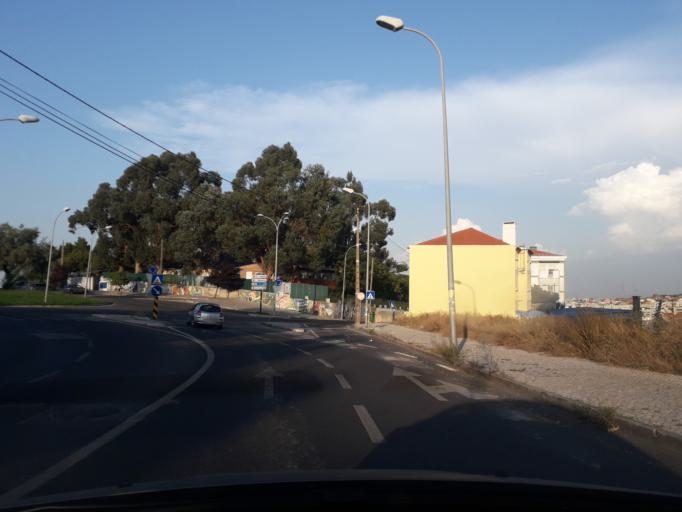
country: PT
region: Lisbon
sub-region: Amadora
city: Amadora
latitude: 38.7446
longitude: -9.2267
